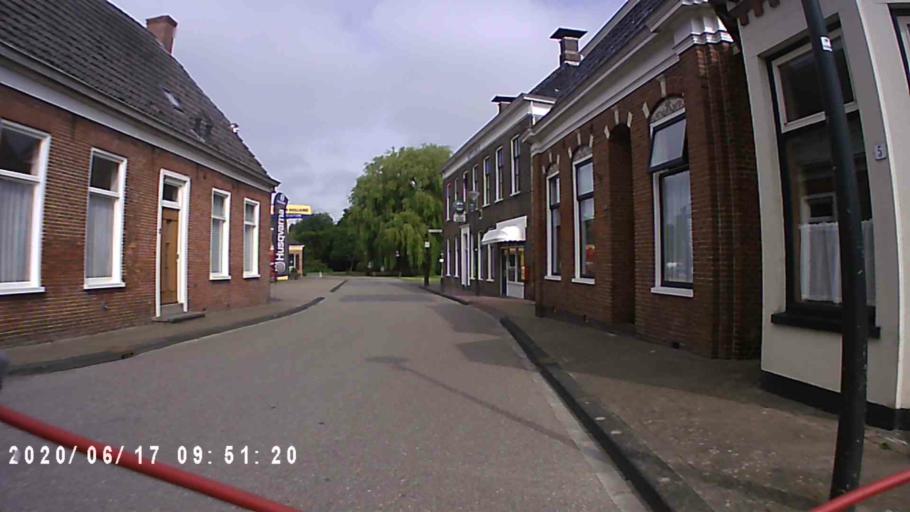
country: NL
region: Groningen
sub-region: Gemeente De Marne
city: Ulrum
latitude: 53.3594
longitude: 6.3306
